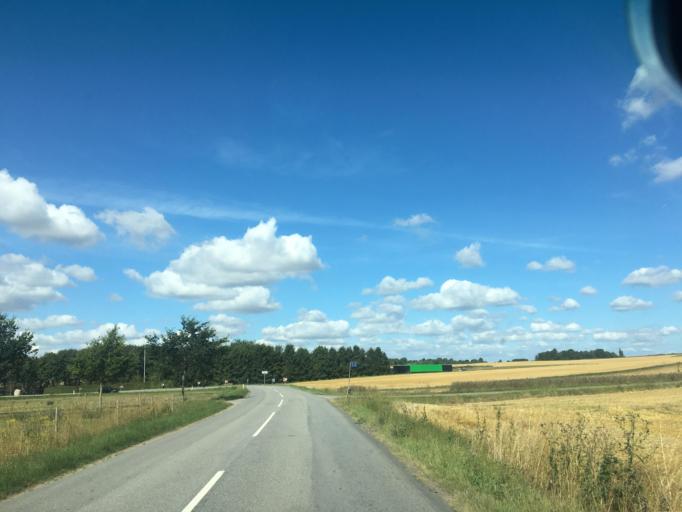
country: DK
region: Zealand
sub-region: Greve Kommune
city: Tune
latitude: 55.5664
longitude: 12.1778
